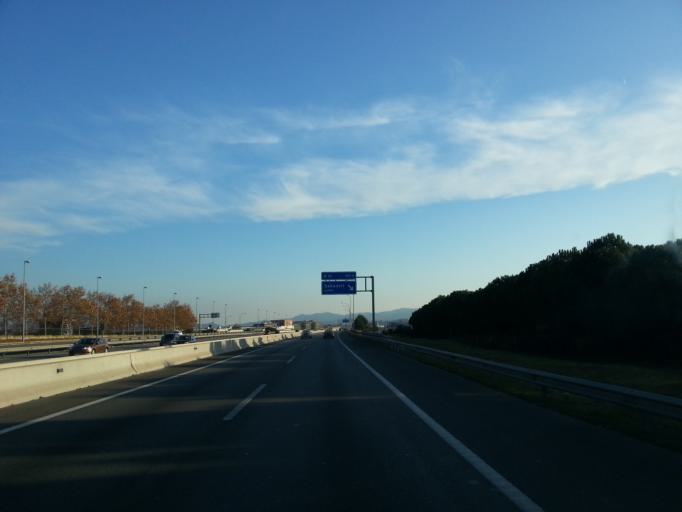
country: ES
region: Catalonia
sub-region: Provincia de Barcelona
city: Sant Quirze del Valles
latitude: 41.5347
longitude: 2.0893
